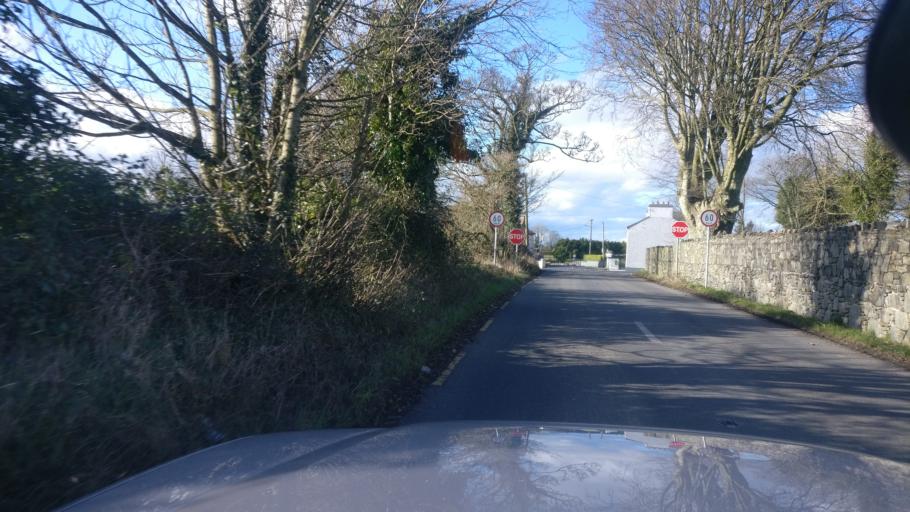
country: IE
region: Connaught
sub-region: County Galway
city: Loughrea
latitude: 53.1960
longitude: -8.3966
